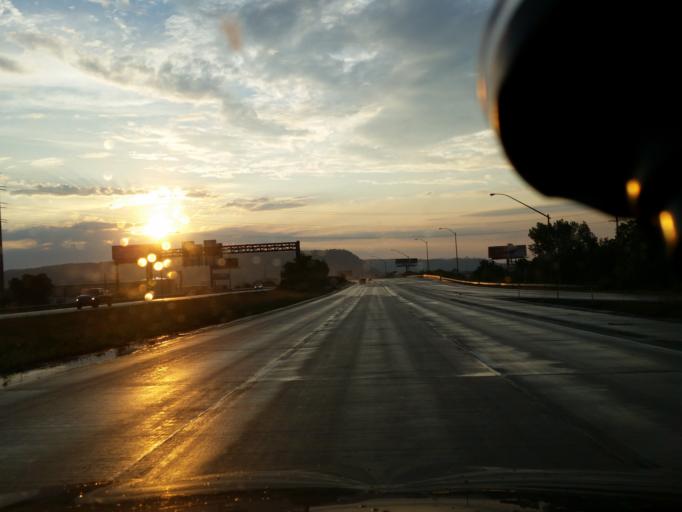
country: US
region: Pennsylvania
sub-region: Dauphin County
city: Harrisburg
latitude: 40.3063
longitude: -76.8852
